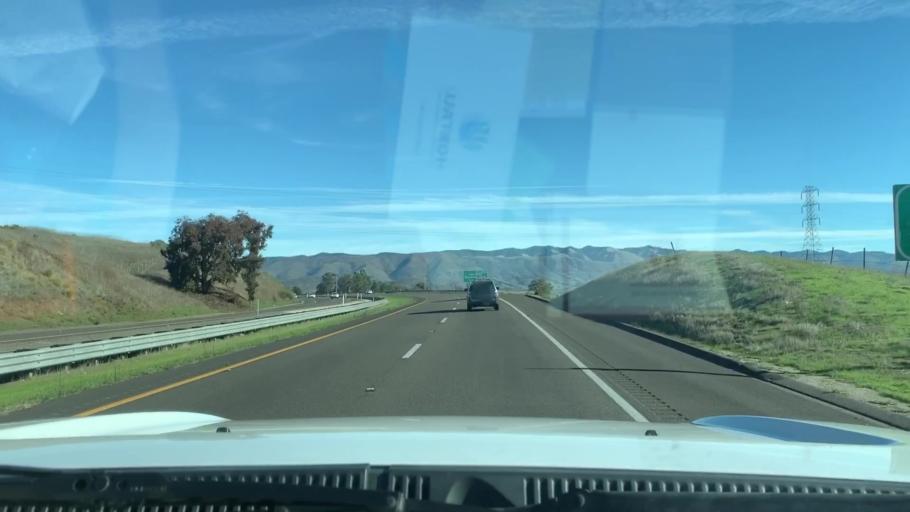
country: US
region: California
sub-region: San Luis Obispo County
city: San Luis Obispo
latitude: 35.2341
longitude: -120.6869
